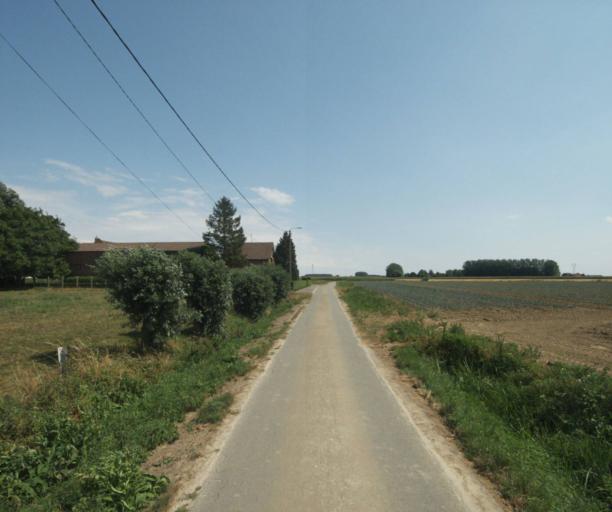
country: FR
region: Nord-Pas-de-Calais
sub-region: Departement du Nord
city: Deulemont
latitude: 50.7396
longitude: 2.9805
